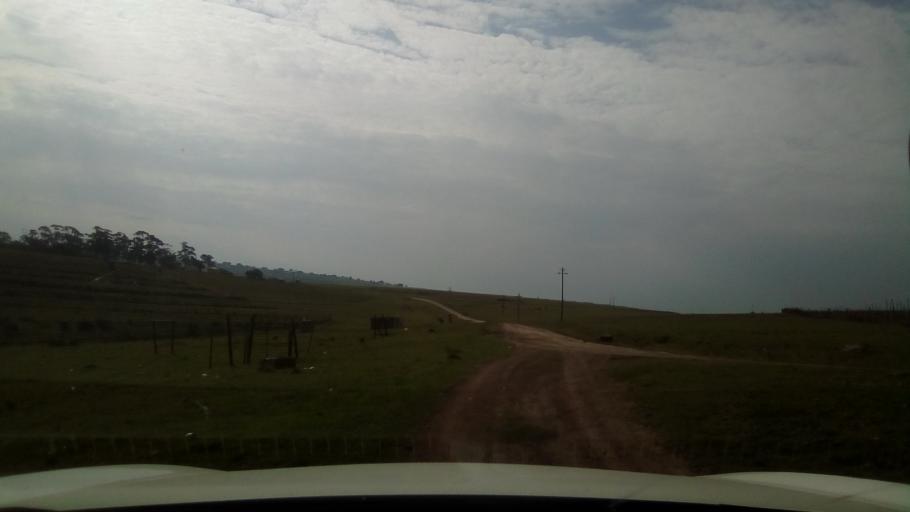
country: ZA
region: Eastern Cape
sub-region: Buffalo City Metropolitan Municipality
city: Bhisho
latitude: -33.0038
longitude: 27.3008
